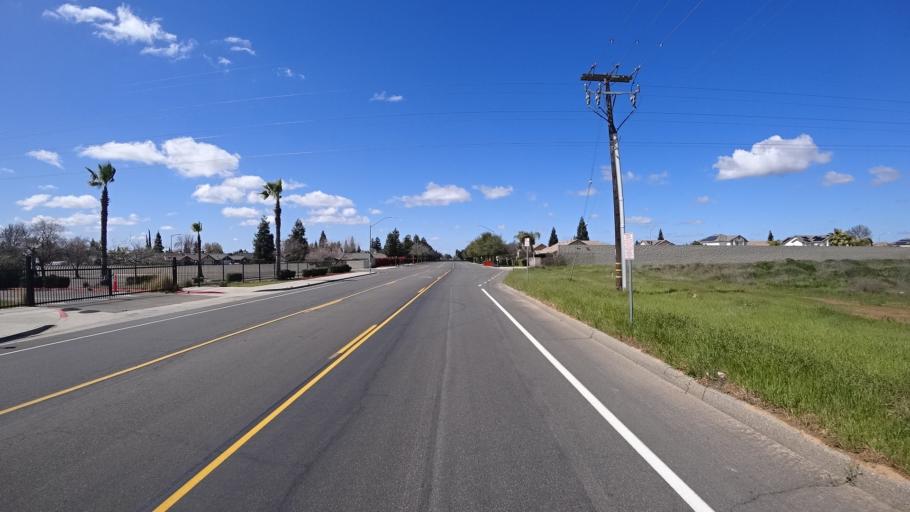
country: US
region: California
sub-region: Fresno County
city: West Park
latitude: 36.8154
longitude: -119.9000
